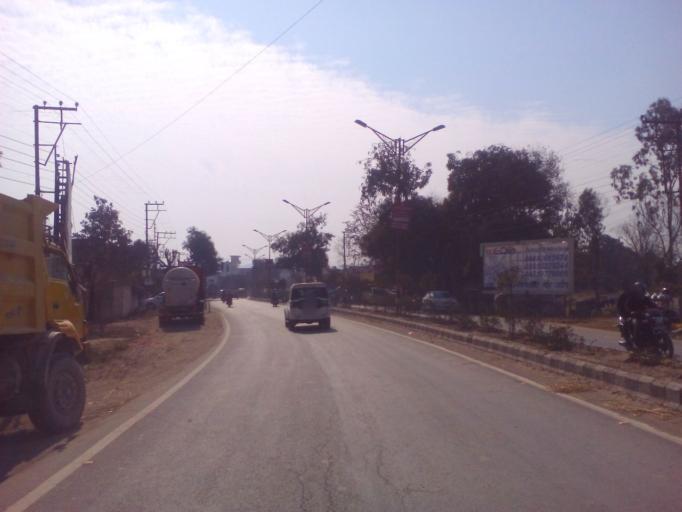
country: IN
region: Uttarakhand
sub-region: Dehradun
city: Clement Town
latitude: 30.2812
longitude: 77.9920
